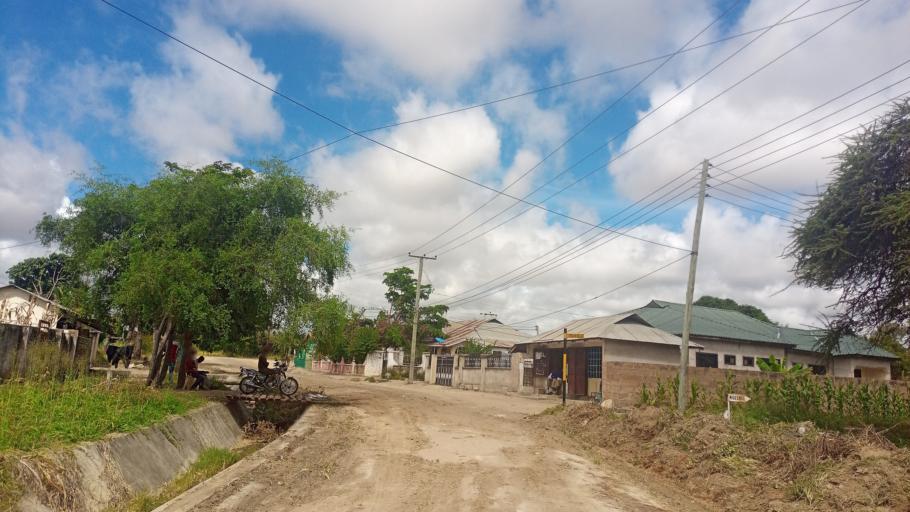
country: TZ
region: Dodoma
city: Dodoma
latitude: -6.1939
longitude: 35.7334
